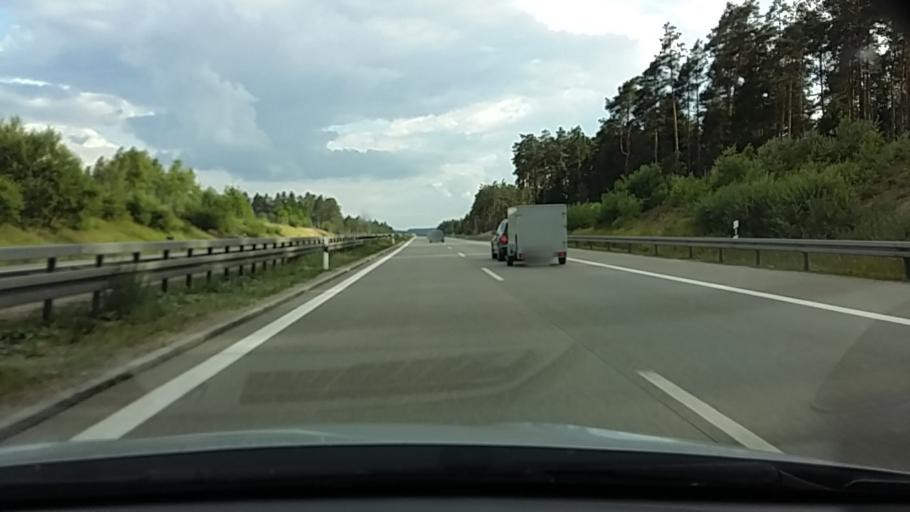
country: DE
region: Bavaria
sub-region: Upper Palatinate
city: Ebermannsdorf
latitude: 49.4168
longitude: 11.9950
